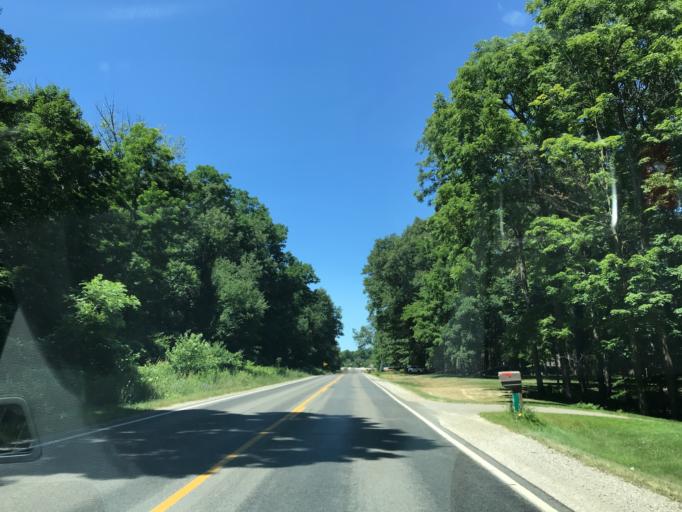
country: US
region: Michigan
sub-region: Livingston County
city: Whitmore Lake
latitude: 42.4679
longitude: -83.7497
